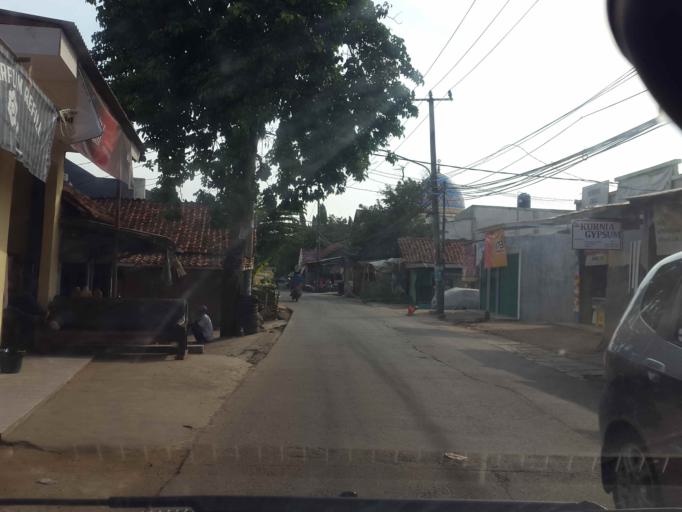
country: ID
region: West Java
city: Serpong
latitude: -6.2777
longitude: 106.6693
